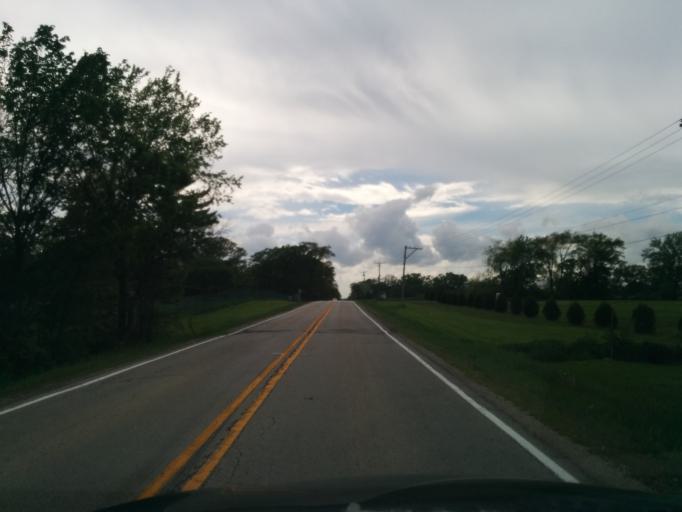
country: US
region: Illinois
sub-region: Cook County
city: Lemont
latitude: 41.6413
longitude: -88.0357
